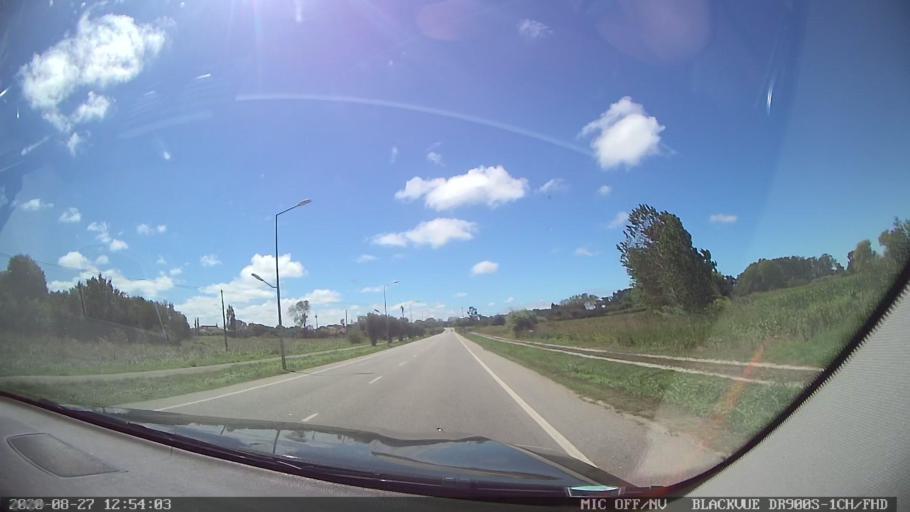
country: PT
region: Aveiro
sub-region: Ilhavo
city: Ilhavo
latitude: 40.5970
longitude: -8.6792
